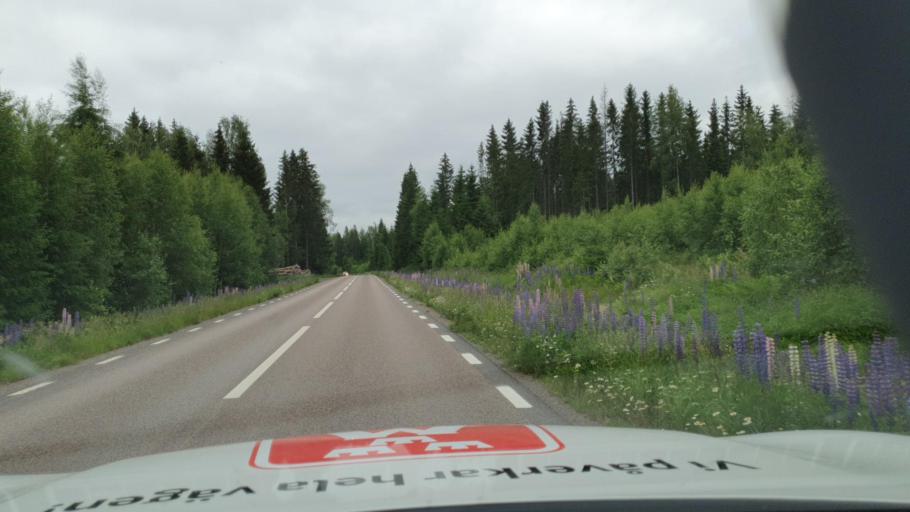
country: SE
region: Vaermland
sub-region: Sunne Kommun
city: Sunne
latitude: 59.9062
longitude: 12.9058
